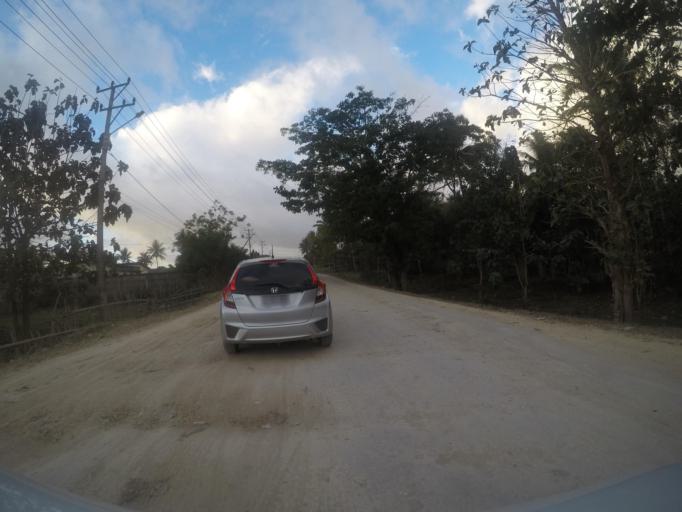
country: TL
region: Lautem
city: Lospalos
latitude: -8.5101
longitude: 126.9866
